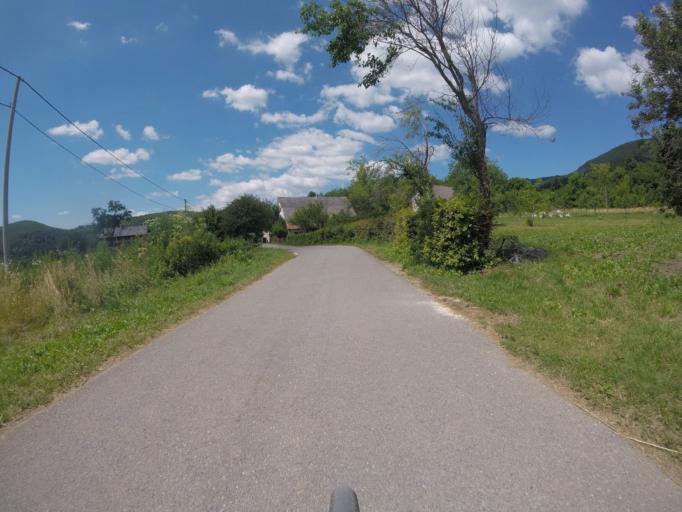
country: SI
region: Kostanjevica na Krki
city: Kostanjevica na Krki
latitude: 45.7533
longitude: 15.3861
